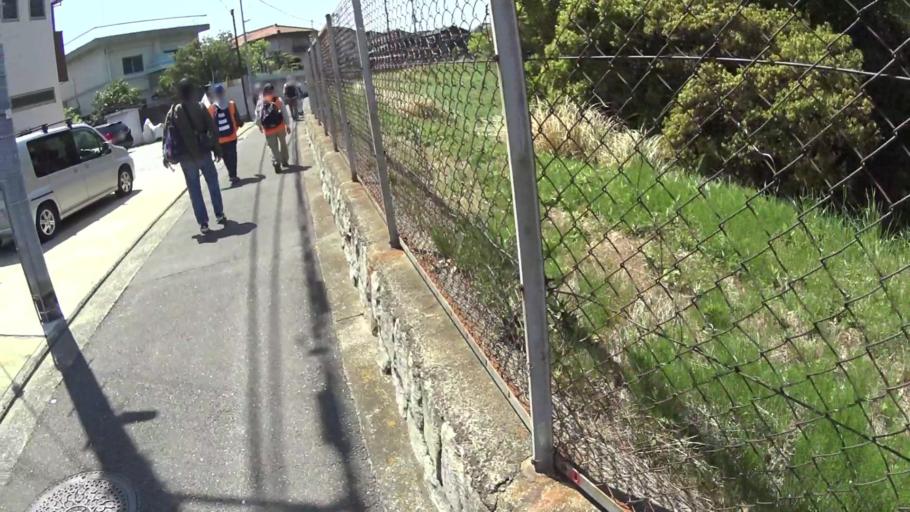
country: JP
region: Osaka
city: Kashihara
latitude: 34.5707
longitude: 135.6143
